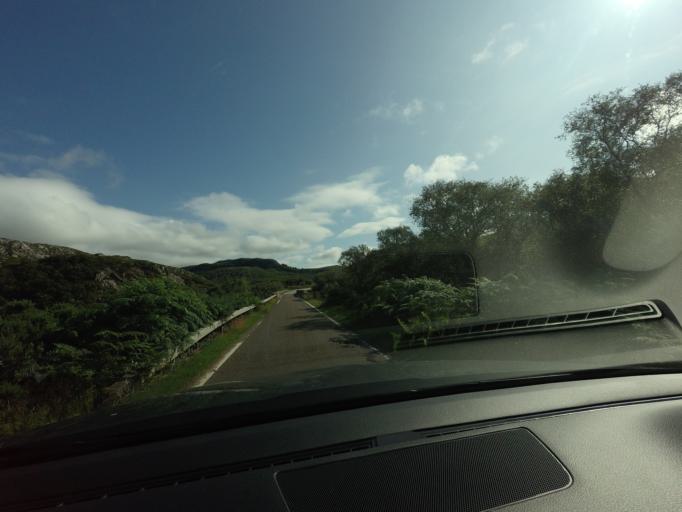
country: GB
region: Scotland
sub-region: Highland
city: Ullapool
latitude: 58.3752
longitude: -5.0168
